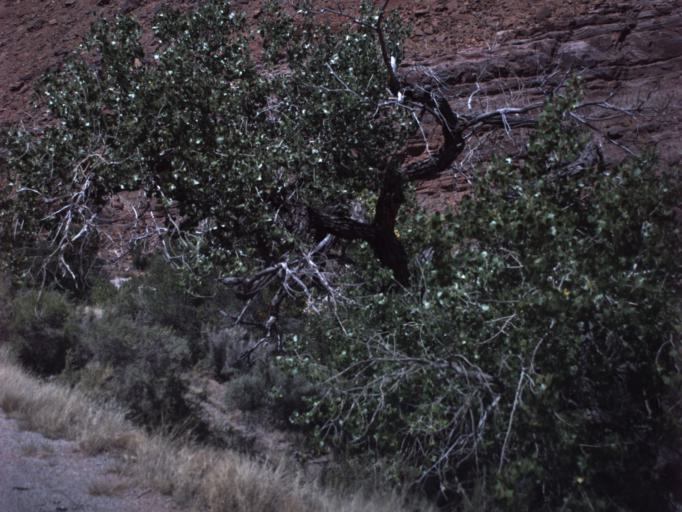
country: US
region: Utah
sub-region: Grand County
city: Moab
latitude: 38.6841
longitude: -109.4589
